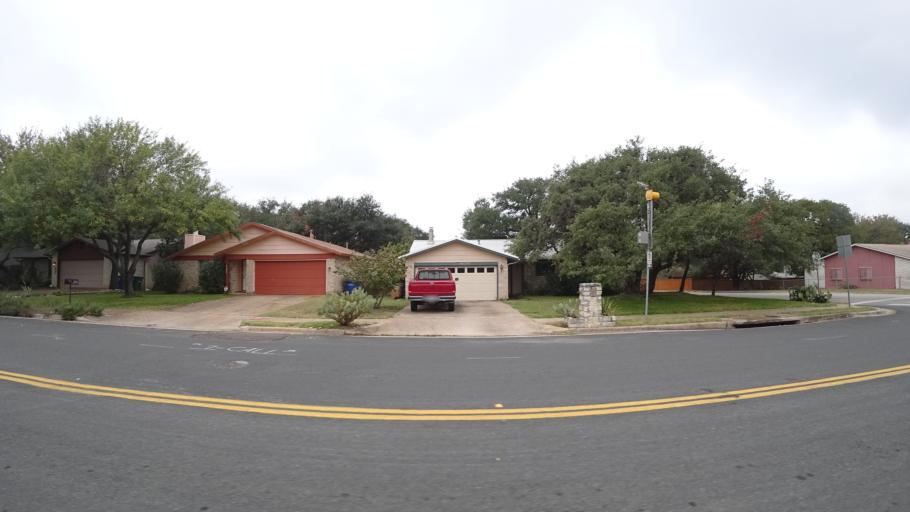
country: US
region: Texas
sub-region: Travis County
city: Shady Hollow
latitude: 30.2047
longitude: -97.8406
